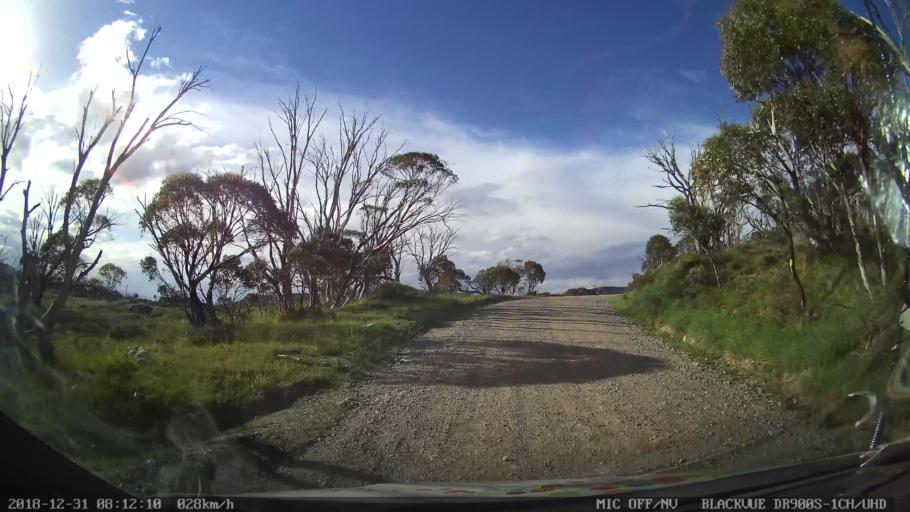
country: AU
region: New South Wales
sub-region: Snowy River
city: Jindabyne
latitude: -36.3863
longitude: 148.4302
